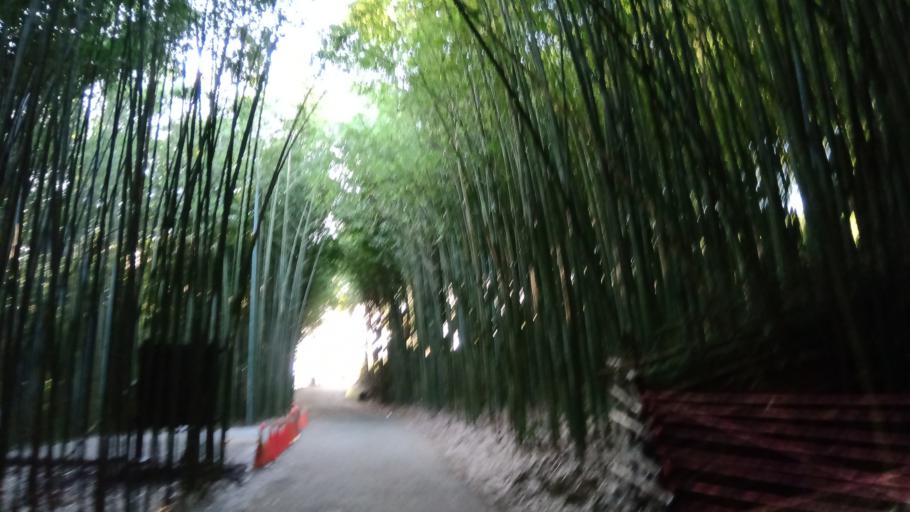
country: TW
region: Taiwan
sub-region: Miaoli
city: Miaoli
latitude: 24.4206
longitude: 120.9201
